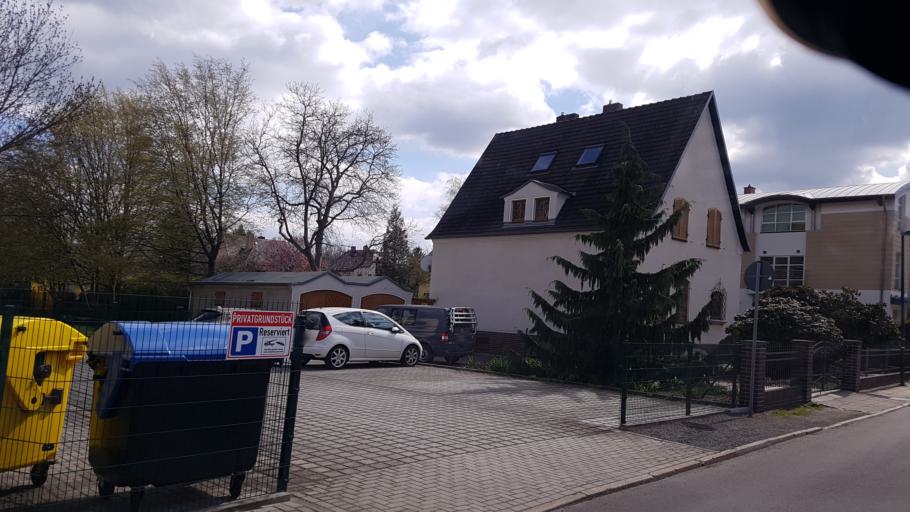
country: DE
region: Brandenburg
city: Senftenberg
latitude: 51.5221
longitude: 14.0078
